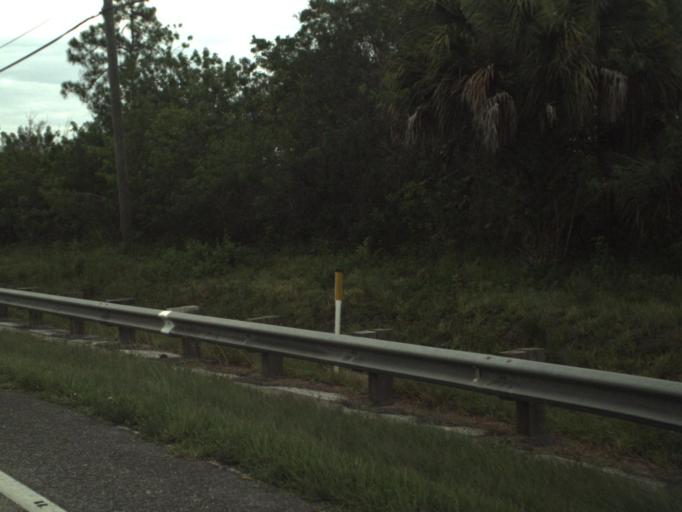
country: US
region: Florida
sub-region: Palm Beach County
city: Loxahatchee Groves
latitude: 26.6826
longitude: -80.2827
